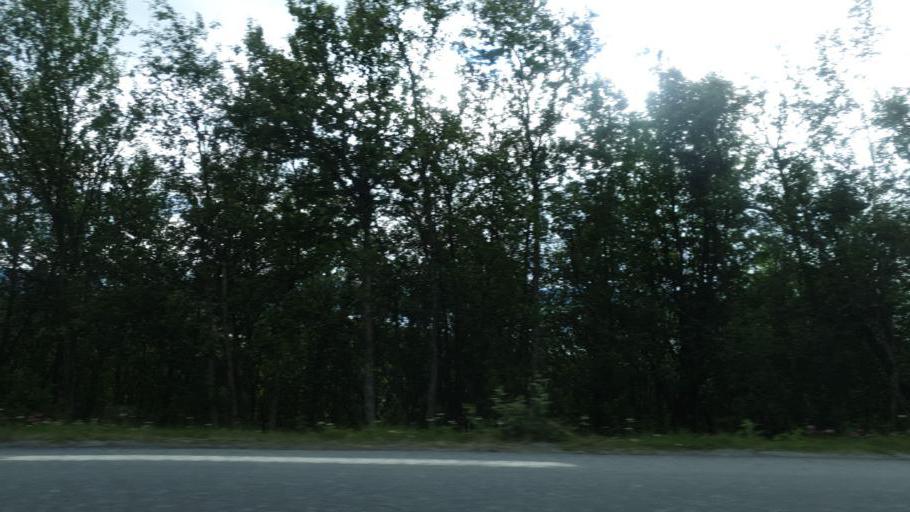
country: NO
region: Oppland
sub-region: Vestre Slidre
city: Slidre
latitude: 61.2500
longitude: 8.8882
